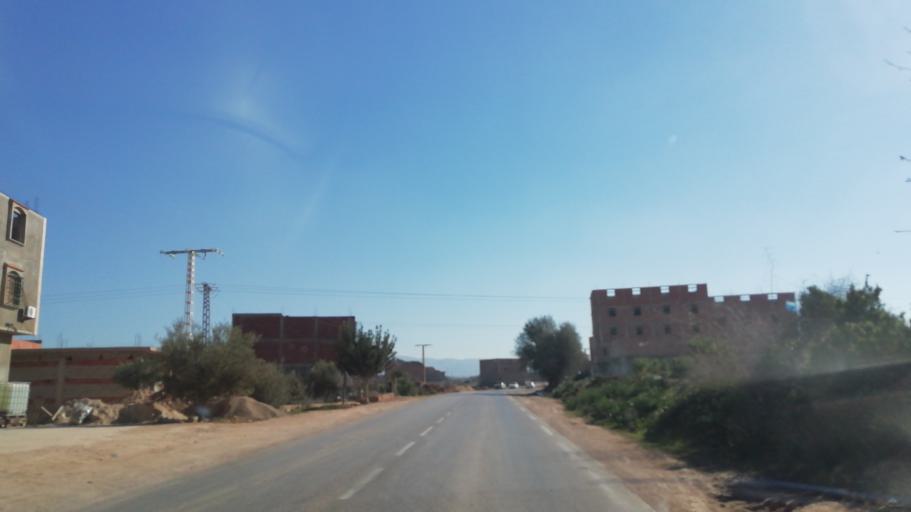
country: DZ
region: Tlemcen
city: Nedroma
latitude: 34.8355
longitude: -1.6994
